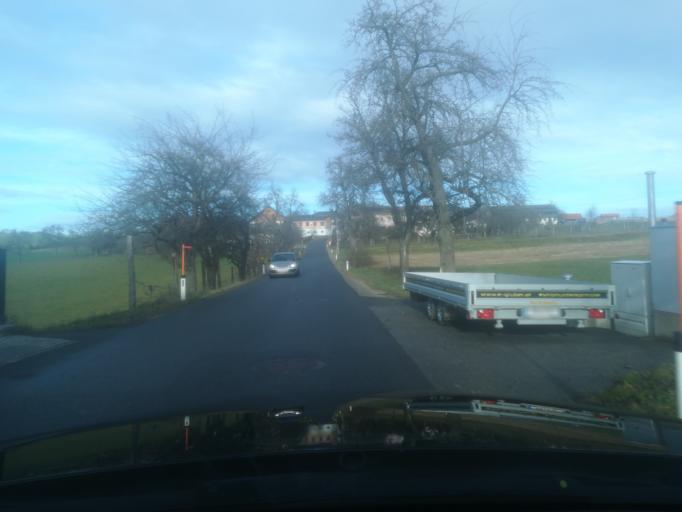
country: AT
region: Upper Austria
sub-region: Politischer Bezirk Perg
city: Perg
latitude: 48.3667
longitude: 14.6320
